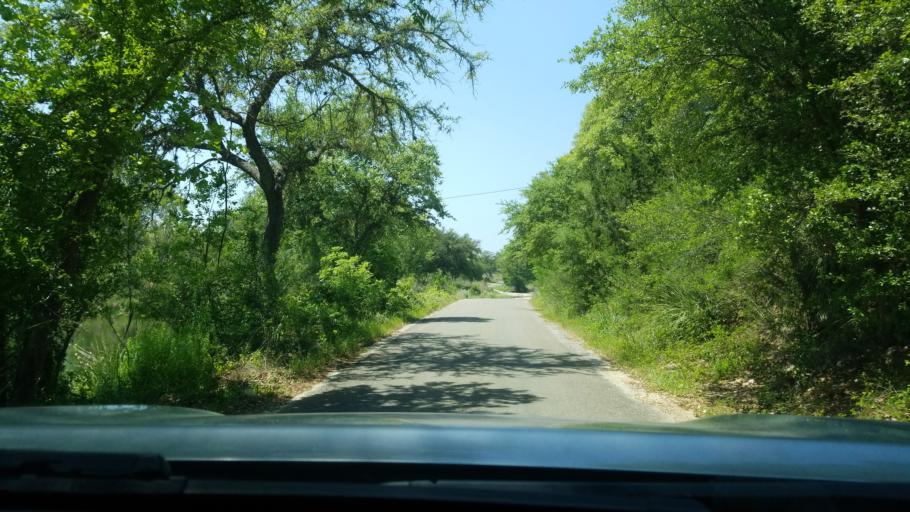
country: US
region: Texas
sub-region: Blanco County
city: Blanco
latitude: 29.9993
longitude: -98.4210
